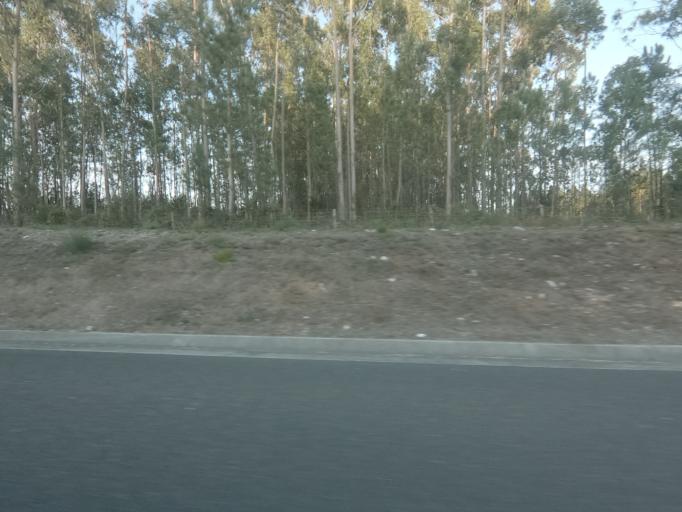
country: PT
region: Leiria
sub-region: Leiria
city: Santa Catarina da Serra
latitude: 39.6415
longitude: -8.6991
